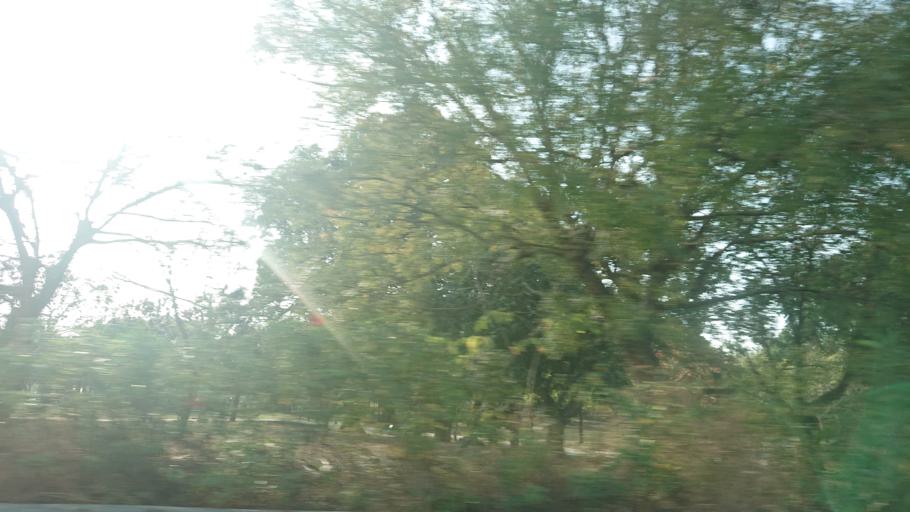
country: TW
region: Taiwan
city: Xinying
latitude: 23.1901
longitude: 120.2714
